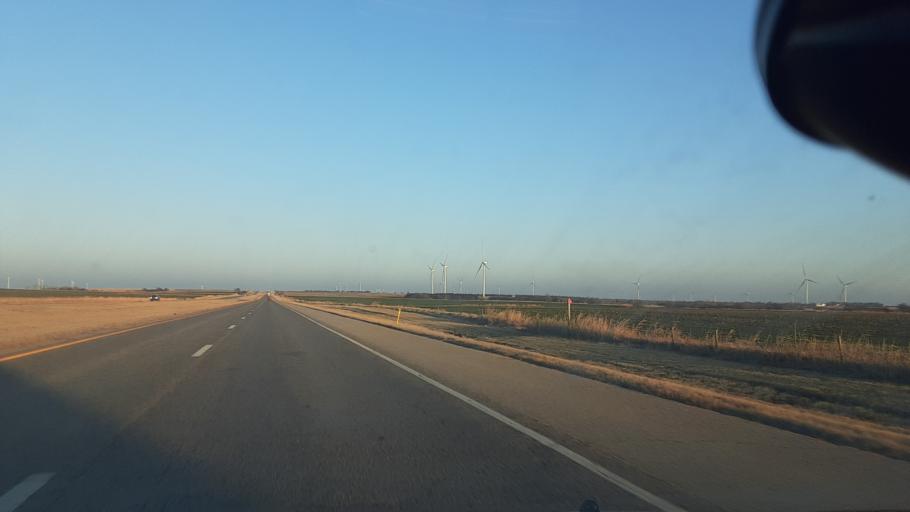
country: US
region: Oklahoma
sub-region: Noble County
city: Perry
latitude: 36.3977
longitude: -97.4755
